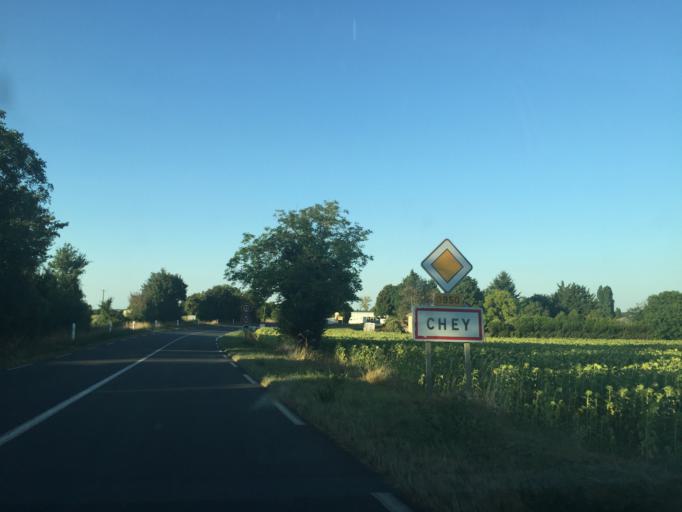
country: FR
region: Poitou-Charentes
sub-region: Departement des Deux-Sevres
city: Lezay
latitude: 46.2966
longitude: -0.0622
